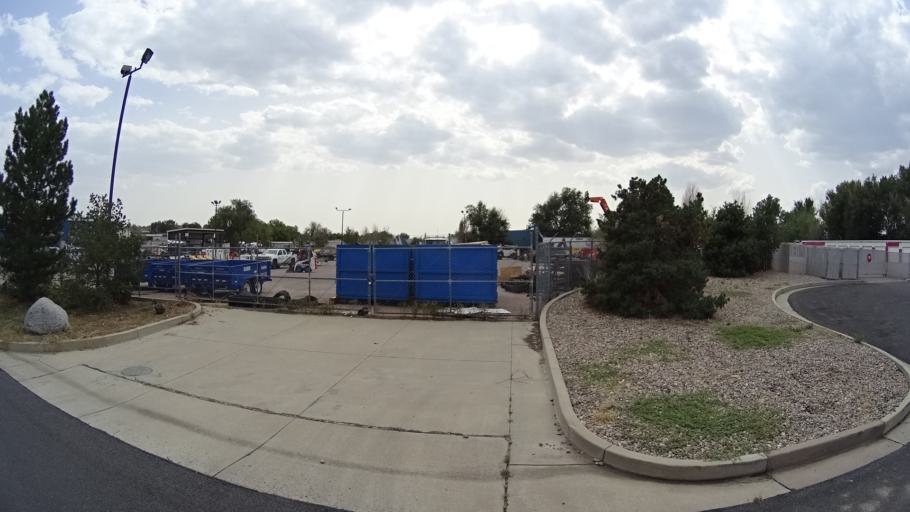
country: US
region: Colorado
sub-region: El Paso County
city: Colorado Springs
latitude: 38.8394
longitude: -104.7649
